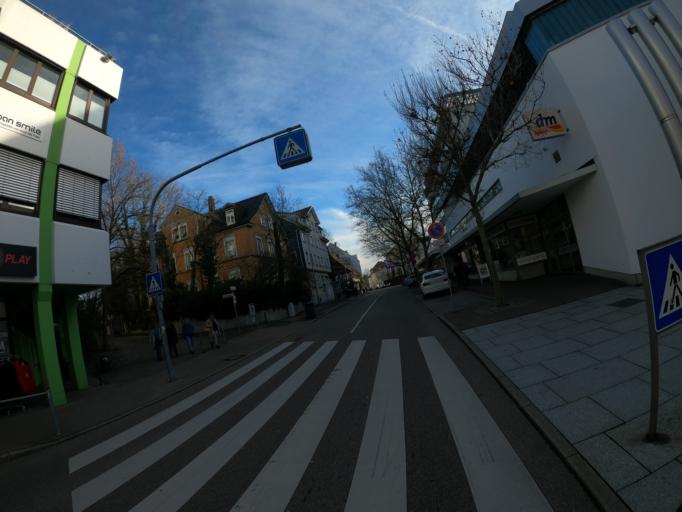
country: DE
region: Baden-Wuerttemberg
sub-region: Regierungsbezirk Stuttgart
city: Goeppingen
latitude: 48.7044
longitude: 9.6552
